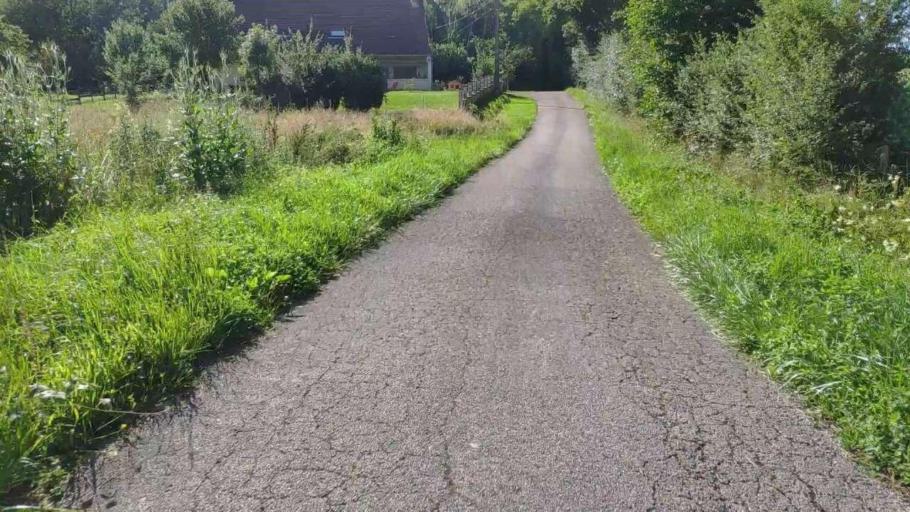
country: FR
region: Franche-Comte
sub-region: Departement du Jura
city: Bletterans
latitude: 46.8229
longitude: 5.4977
